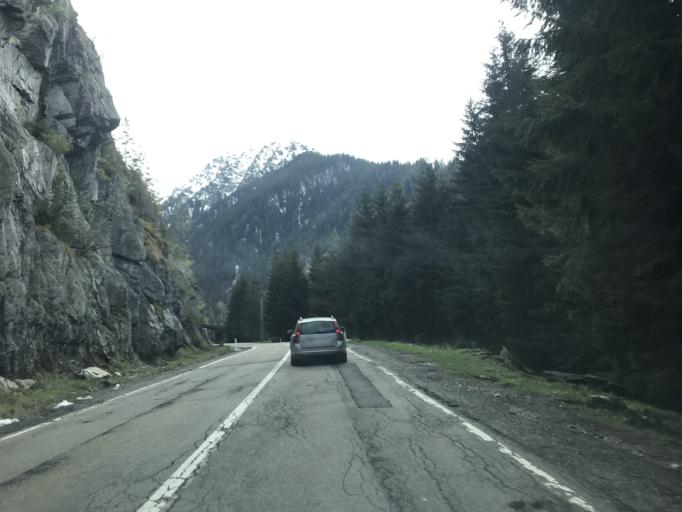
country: RO
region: Sibiu
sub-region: Comuna Cartisoara
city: Cartisoara
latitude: 45.6424
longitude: 24.6054
